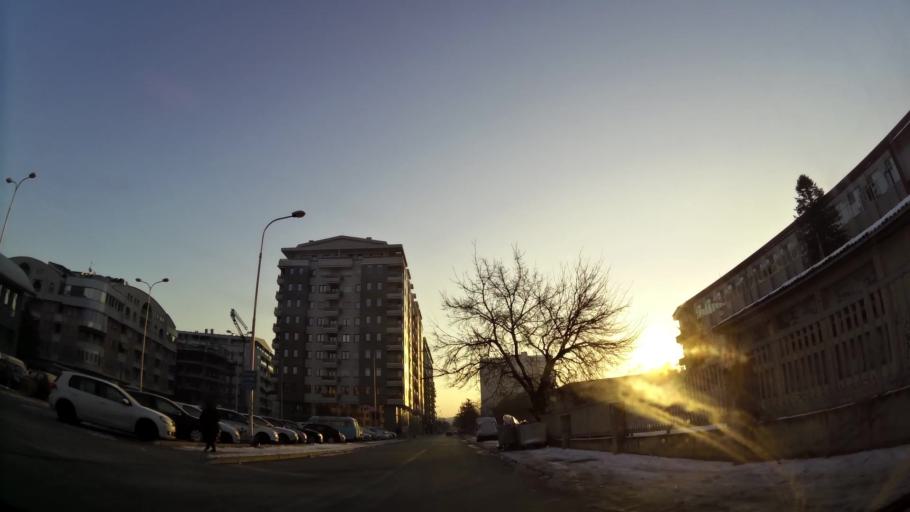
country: MK
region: Karpos
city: Skopje
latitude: 42.0056
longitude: 21.4080
